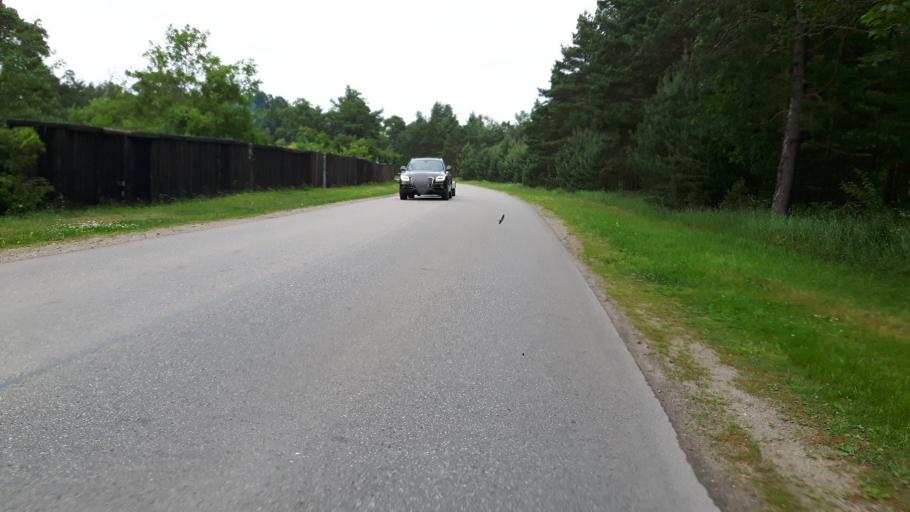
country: LV
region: Liepaja
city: Vec-Liepaja
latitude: 56.5608
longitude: 21.0130
